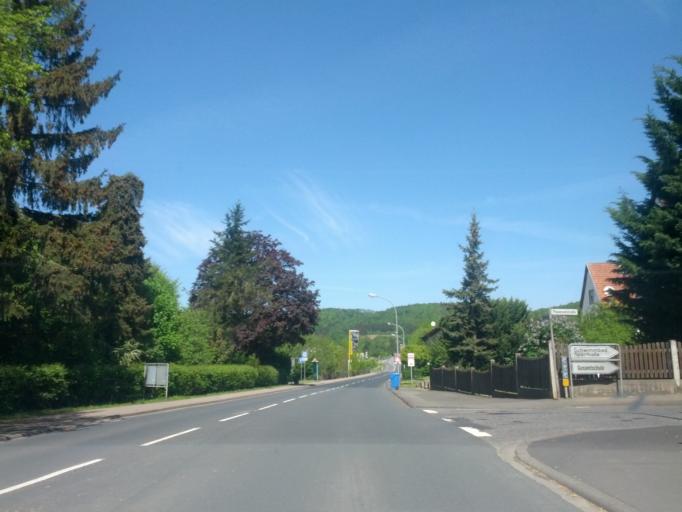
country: DE
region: Hesse
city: Wanfried
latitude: 51.1862
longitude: 10.1687
